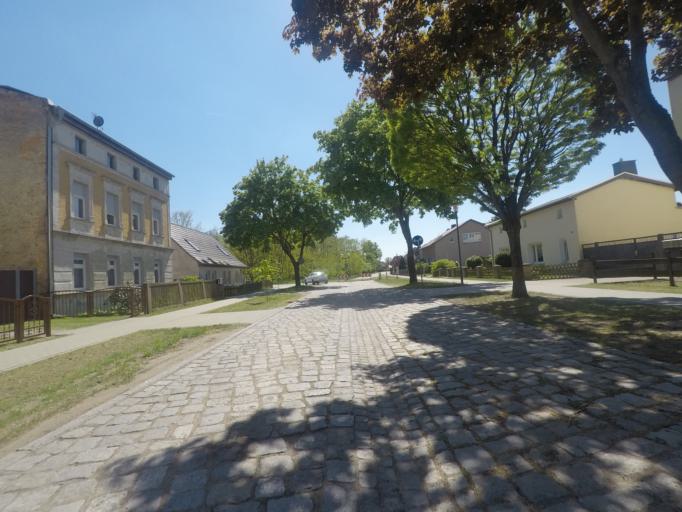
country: DE
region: Brandenburg
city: Melchow
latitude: 52.8408
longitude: 13.6825
